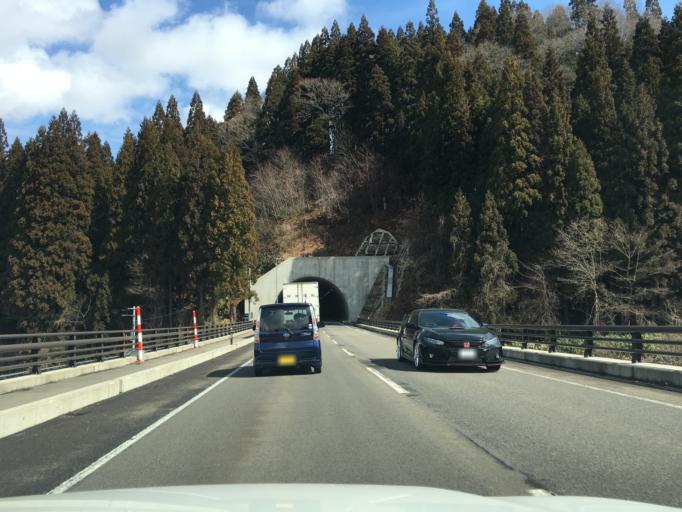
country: JP
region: Akita
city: Takanosu
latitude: 40.1129
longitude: 140.3713
